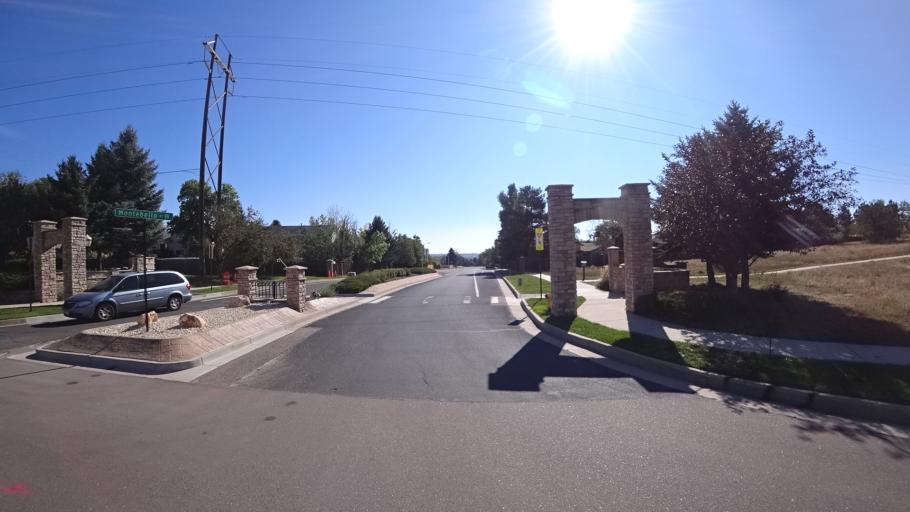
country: US
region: Colorado
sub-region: El Paso County
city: Colorado Springs
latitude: 38.9057
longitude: -104.7897
